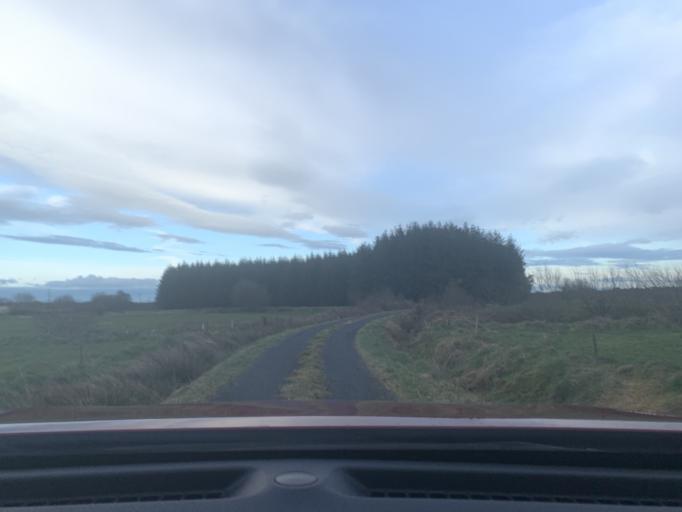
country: IE
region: Connaught
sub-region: Roscommon
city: Ballaghaderreen
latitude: 53.8901
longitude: -8.5831
